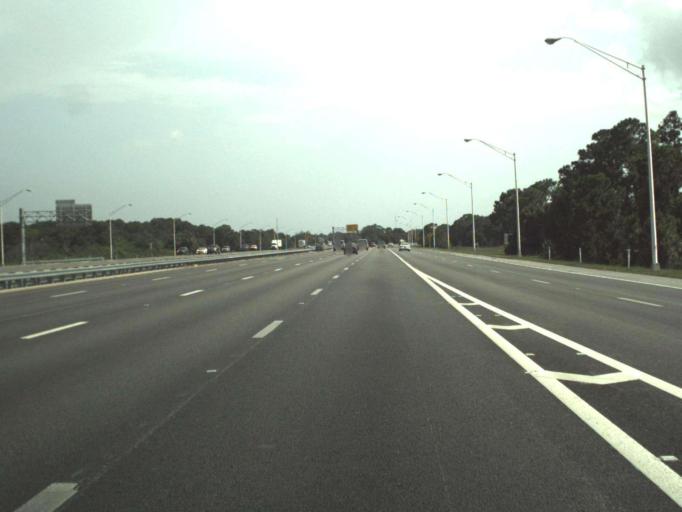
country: US
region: Florida
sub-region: Saint Lucie County
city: Fort Pierce South
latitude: 27.4111
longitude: -80.3887
